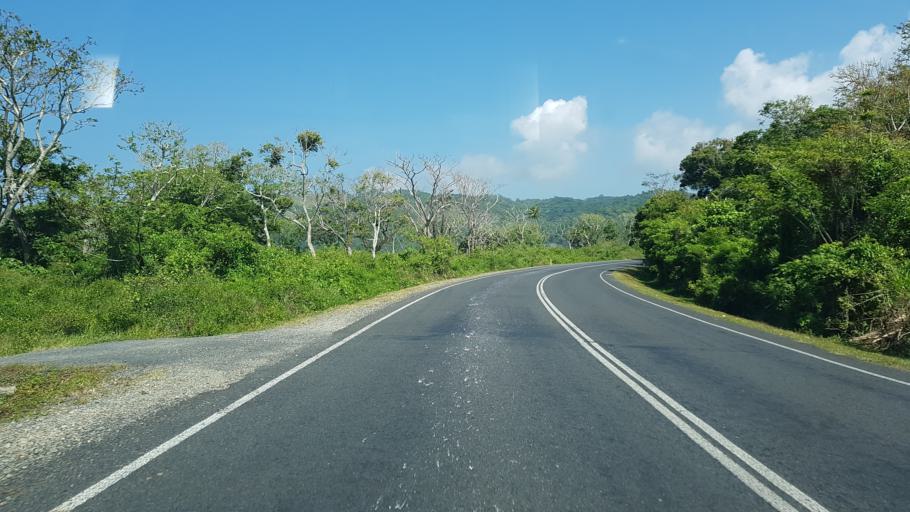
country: FJ
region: Western
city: Nadi
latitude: -18.1833
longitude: 177.5979
